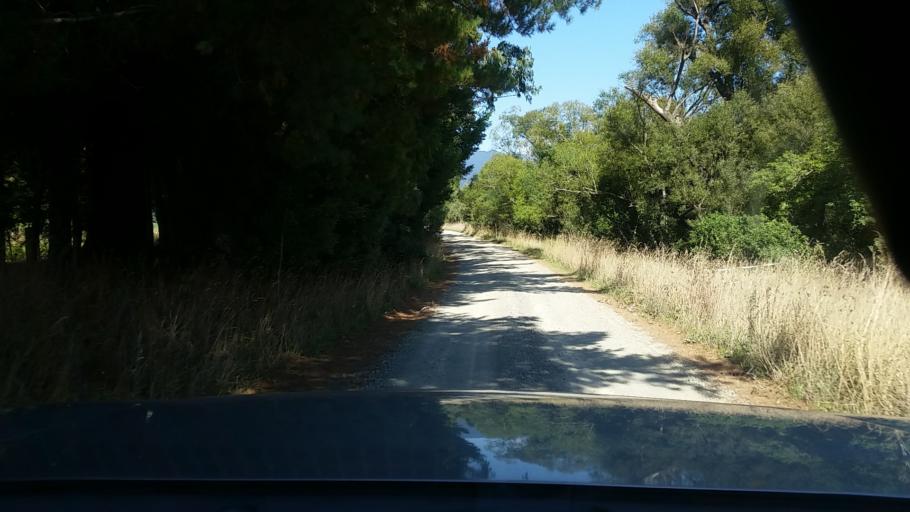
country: NZ
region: Nelson
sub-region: Nelson City
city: Nelson
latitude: -41.2632
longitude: 173.5765
